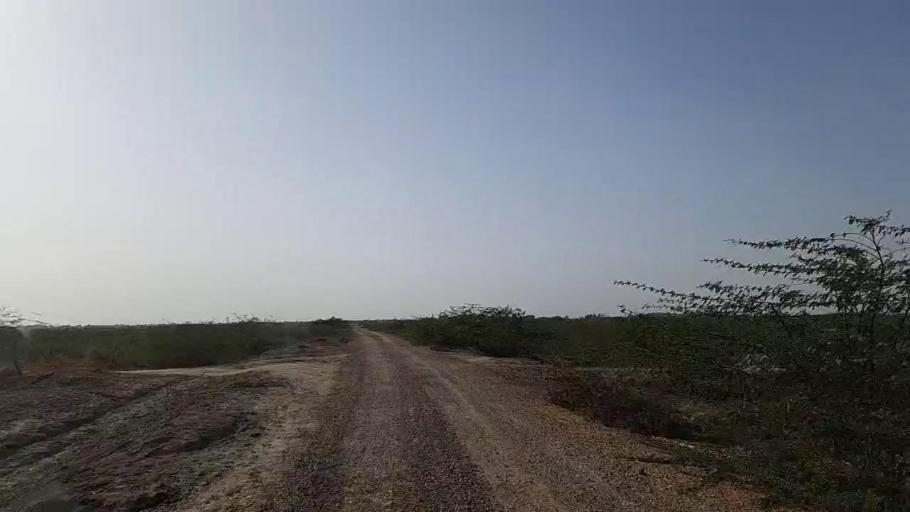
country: PK
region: Sindh
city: Jati
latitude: 24.2847
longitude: 68.2225
